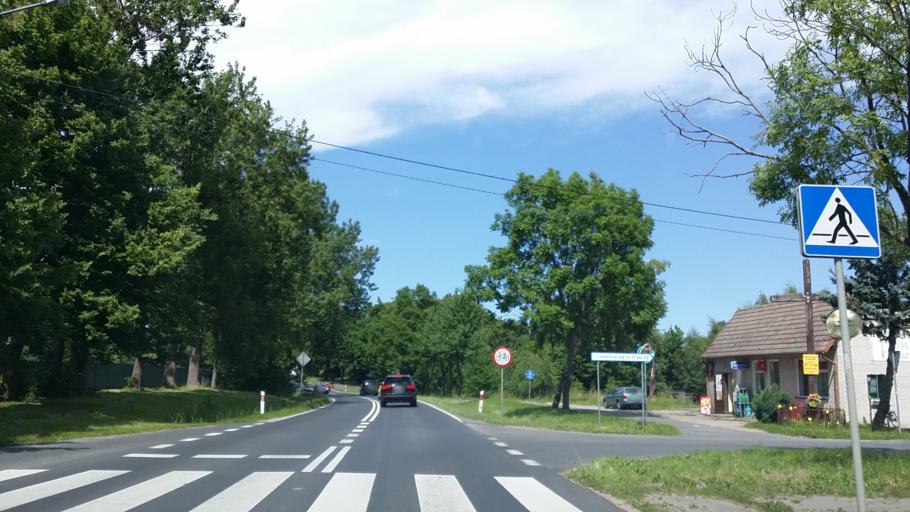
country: PL
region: West Pomeranian Voivodeship
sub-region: Powiat koszalinski
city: Mielno
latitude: 54.2392
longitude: 16.0702
